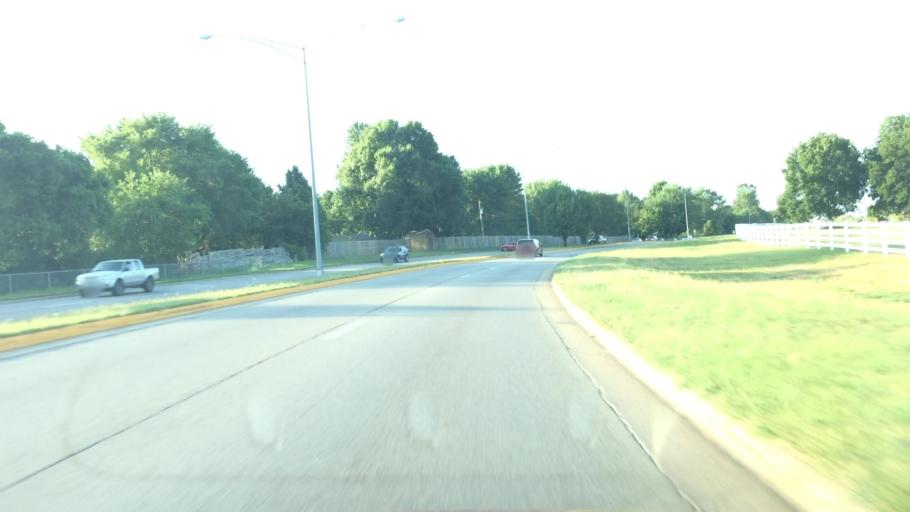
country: US
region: Missouri
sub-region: Greene County
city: Springfield
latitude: 37.1737
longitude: -93.3165
